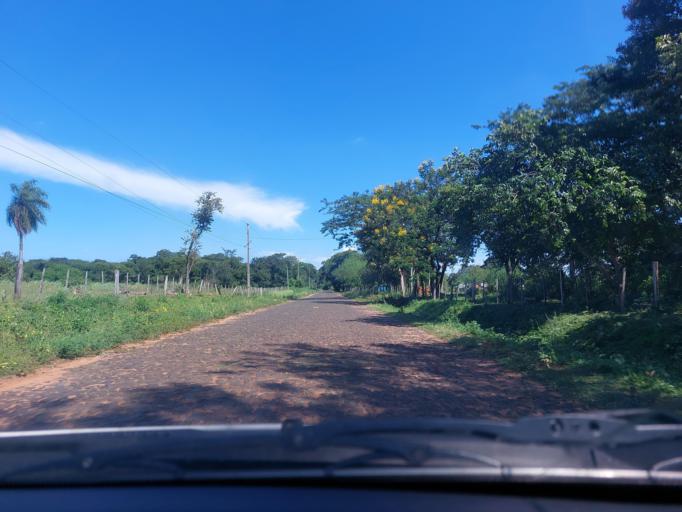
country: PY
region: San Pedro
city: Itacurubi del Rosario
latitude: -24.5745
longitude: -56.5986
